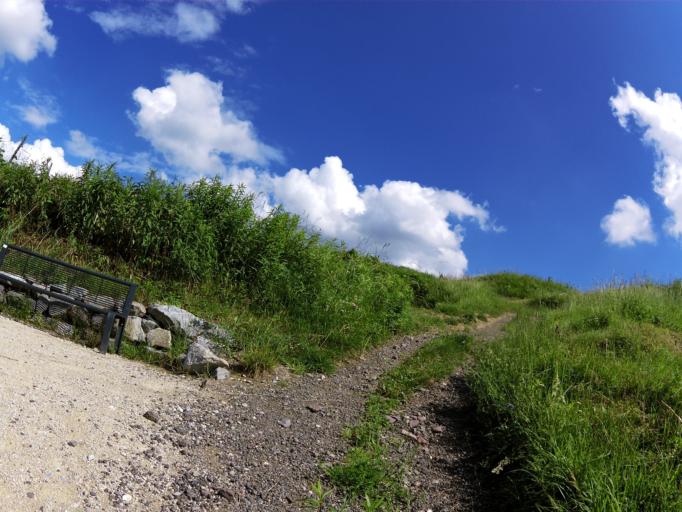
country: DE
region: Baden-Wuerttemberg
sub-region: Freiburg Region
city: Lahr
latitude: 48.3480
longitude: 7.8514
